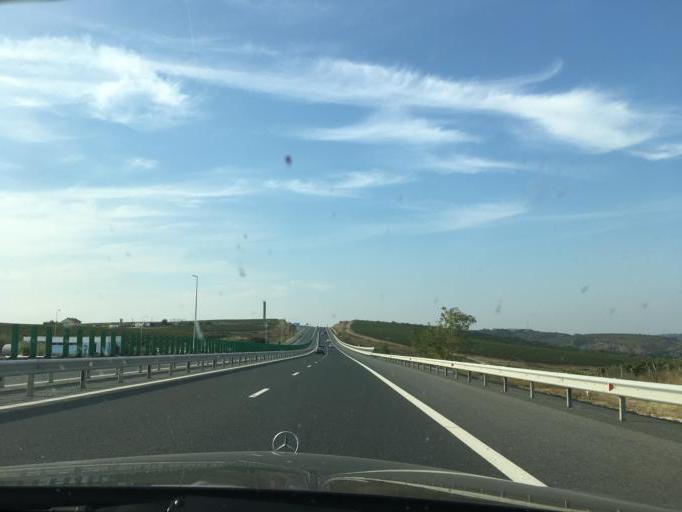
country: RO
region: Constanta
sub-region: Comuna Saligny
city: Saligny
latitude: 44.2836
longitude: 28.0491
